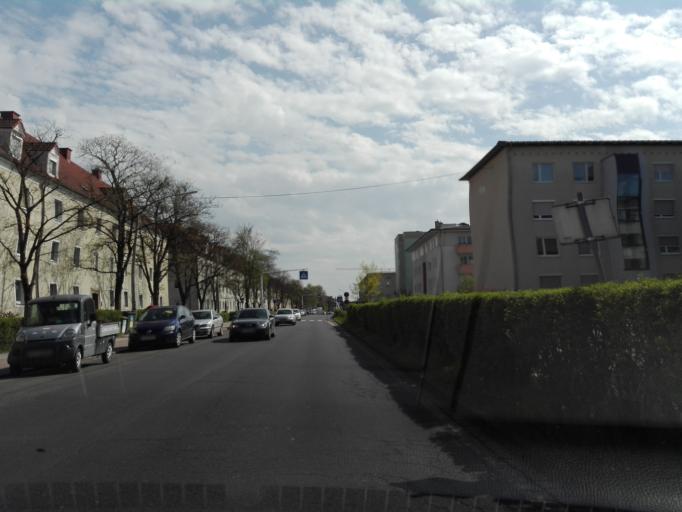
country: AT
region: Upper Austria
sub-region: Politischer Bezirk Linz-Land
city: Leonding
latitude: 48.2520
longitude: 14.2834
